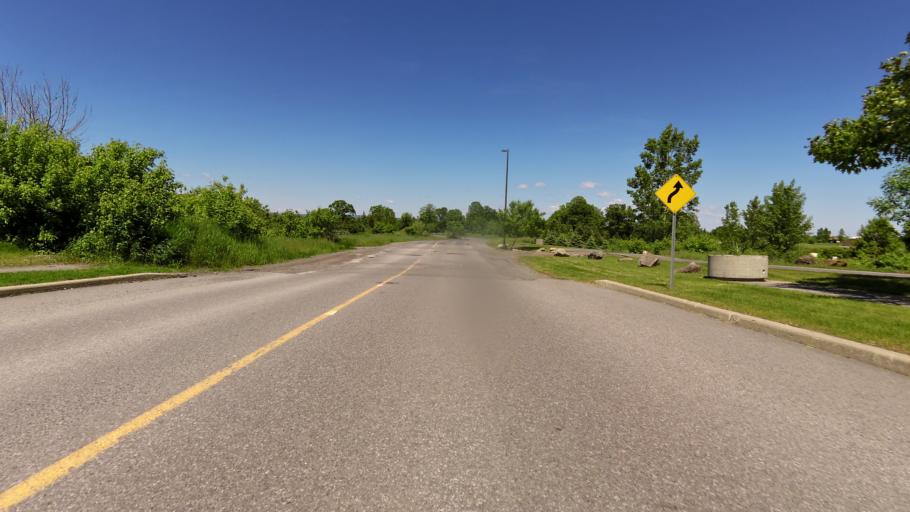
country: CA
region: Ontario
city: Bells Corners
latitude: 45.3531
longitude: -75.9130
